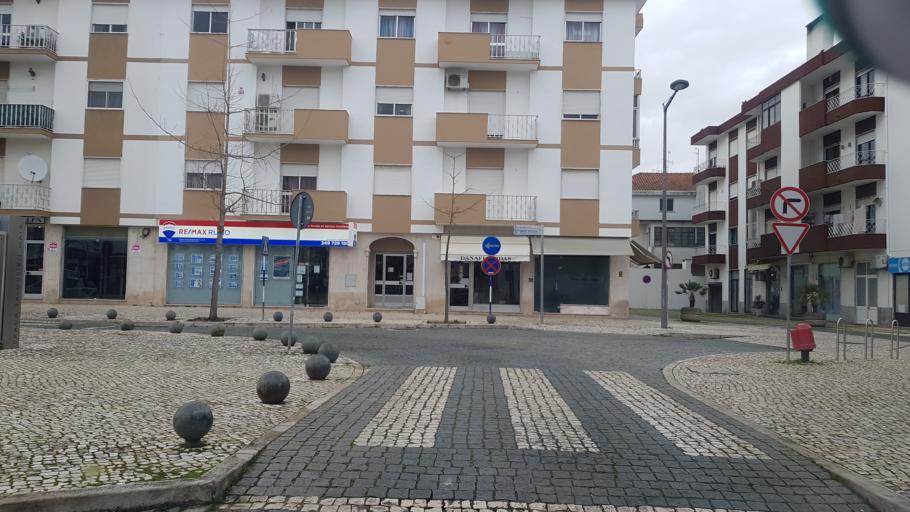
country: PT
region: Santarem
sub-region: Entroncamento
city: Entroncamento
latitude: 39.4624
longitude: -8.4698
